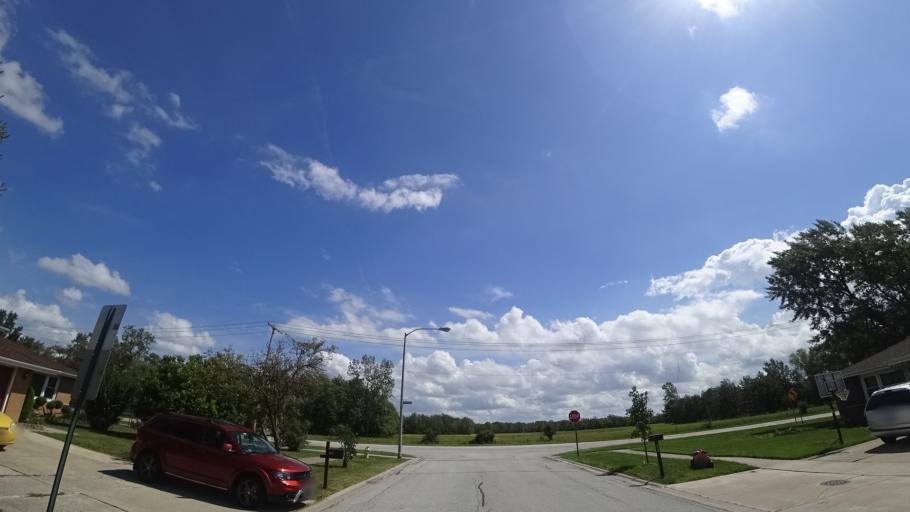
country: US
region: Illinois
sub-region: Cook County
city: Tinley Park
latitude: 41.5616
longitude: -87.7747
